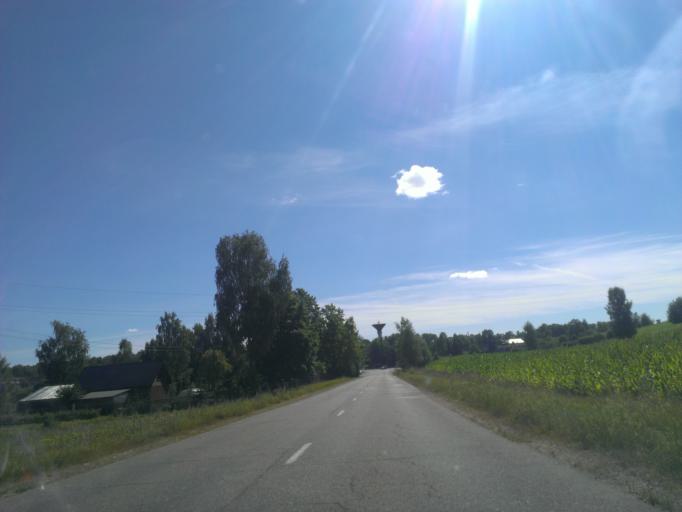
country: LV
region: Malpils
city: Malpils
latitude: 57.0137
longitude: 24.9455
